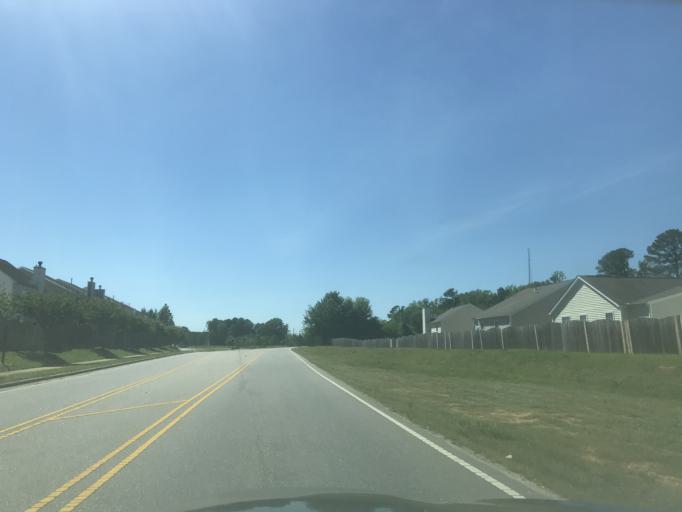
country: US
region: North Carolina
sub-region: Wake County
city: Garner
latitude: 35.7315
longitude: -78.6235
